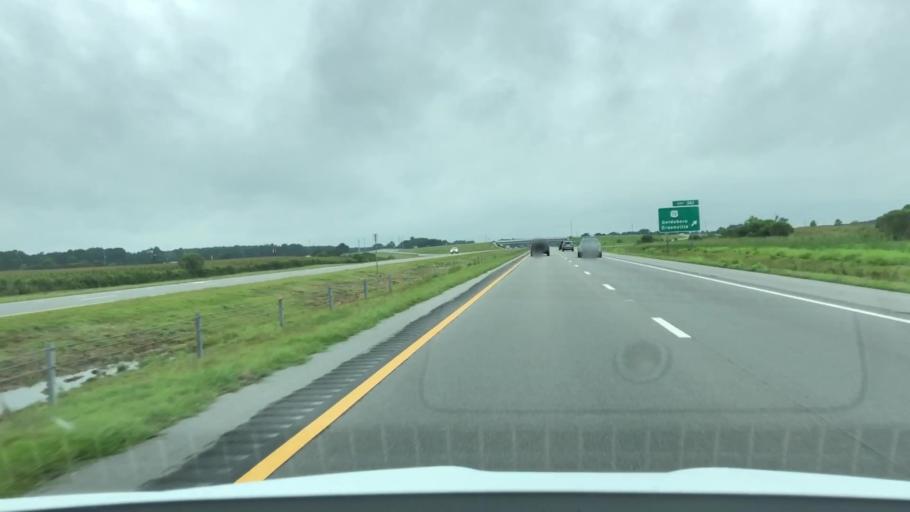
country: US
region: North Carolina
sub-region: Wayne County
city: Elroy
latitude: 35.4093
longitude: -77.8909
